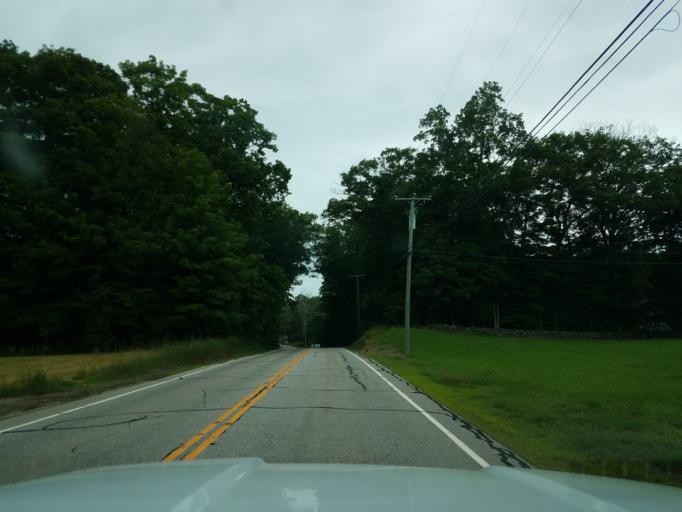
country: US
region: Connecticut
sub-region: Windham County
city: South Woodstock
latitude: 41.9211
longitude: -72.0797
